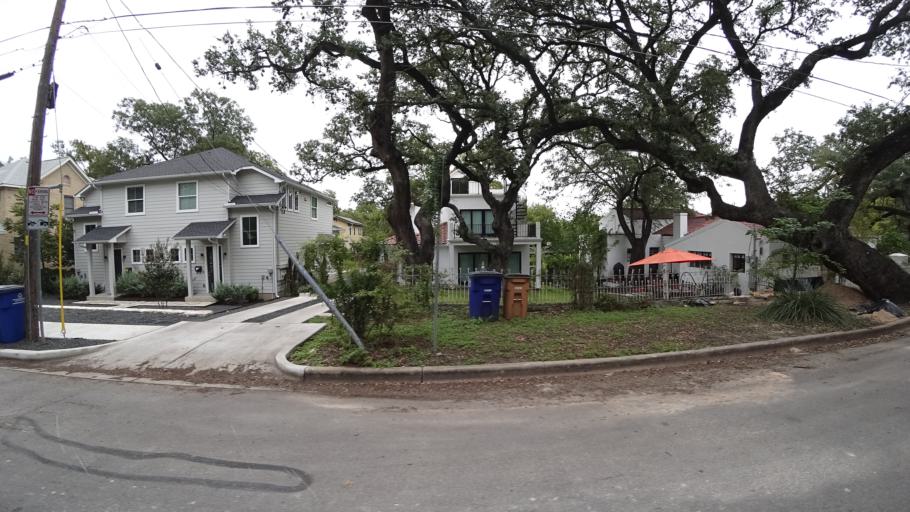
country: US
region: Texas
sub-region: Travis County
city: Austin
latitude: 30.2938
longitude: -97.7317
